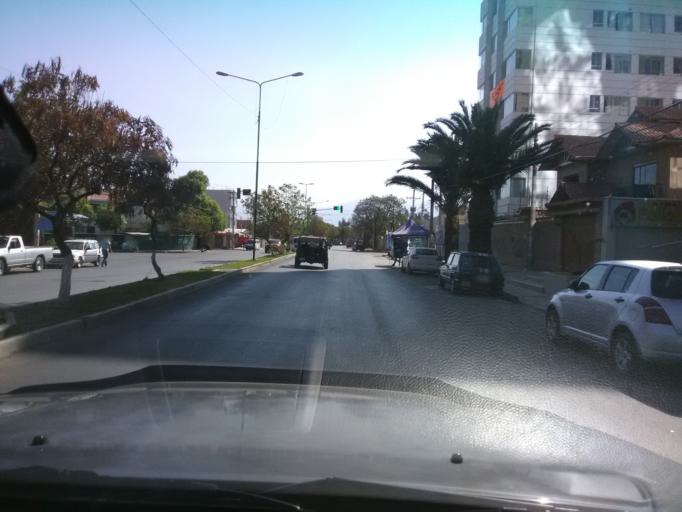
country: BO
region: Cochabamba
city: Cochabamba
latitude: -17.3709
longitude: -66.1880
